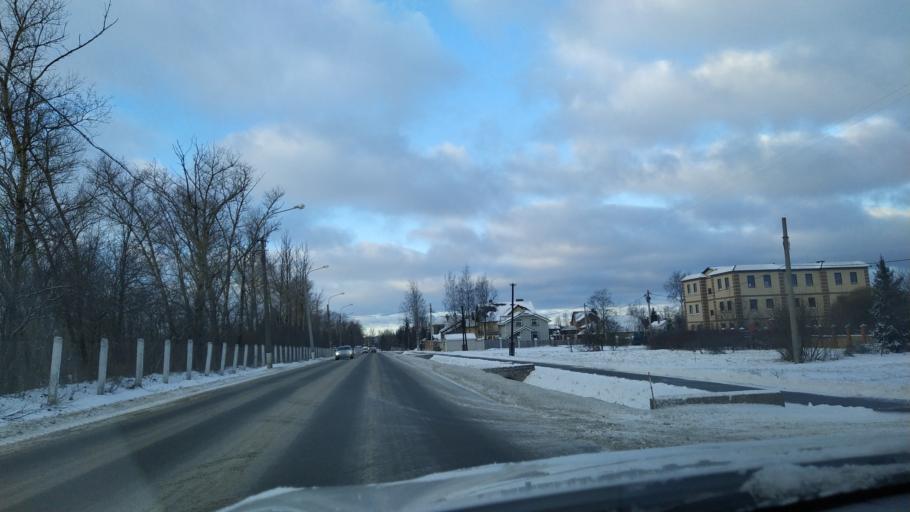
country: RU
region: St.-Petersburg
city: Pushkin
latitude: 59.7311
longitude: 30.3688
